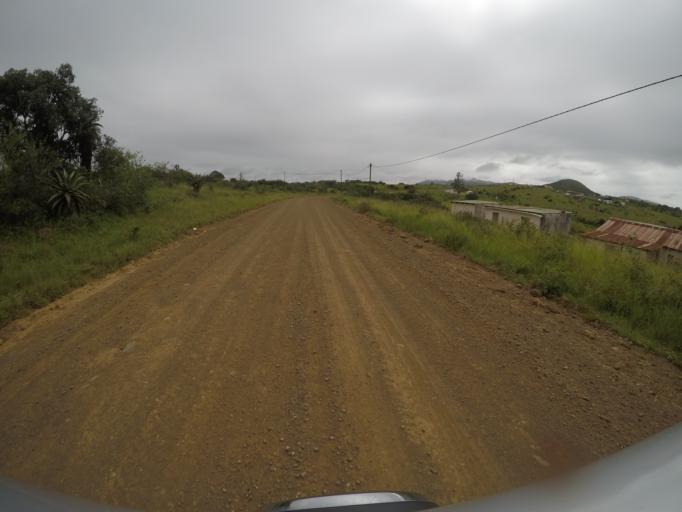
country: ZA
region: KwaZulu-Natal
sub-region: uThungulu District Municipality
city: Empangeni
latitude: -28.6044
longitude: 31.8381
